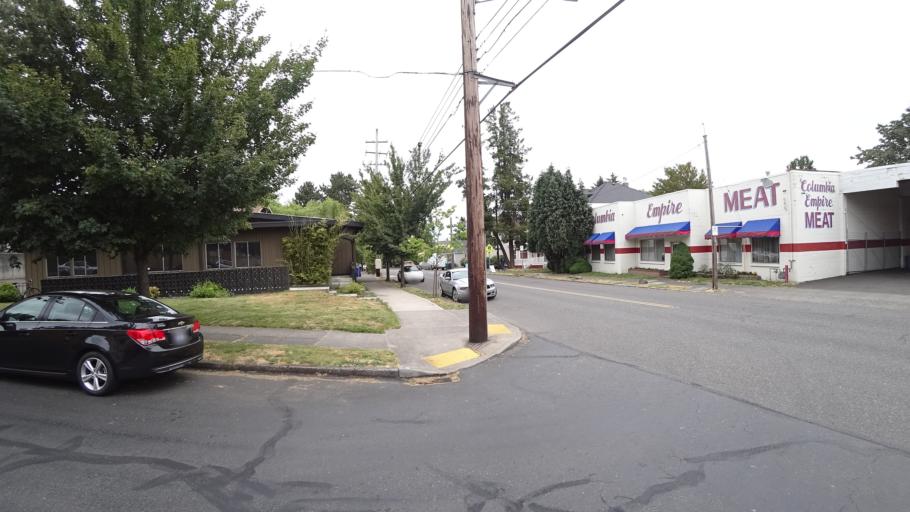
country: US
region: Oregon
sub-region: Multnomah County
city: Portland
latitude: 45.4950
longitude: -122.6532
